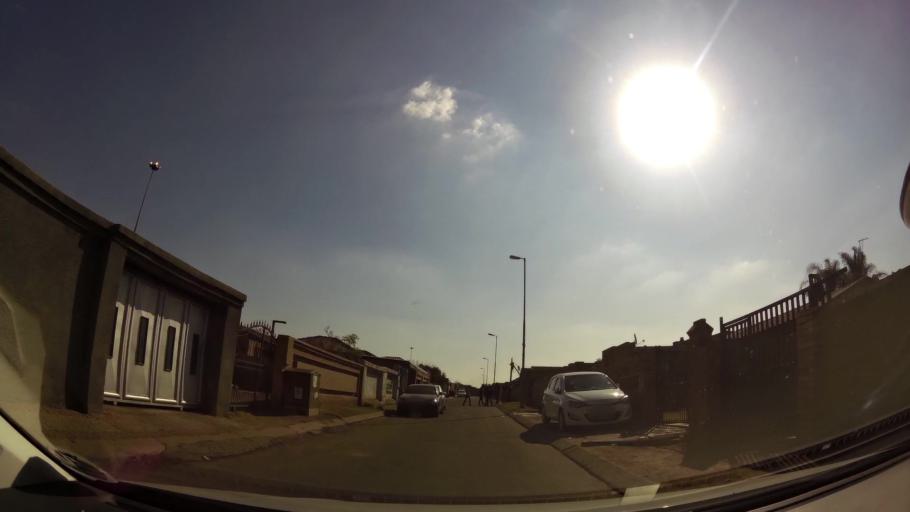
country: ZA
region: Gauteng
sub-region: City of Johannesburg Metropolitan Municipality
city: Soweto
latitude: -26.2813
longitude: 27.8661
